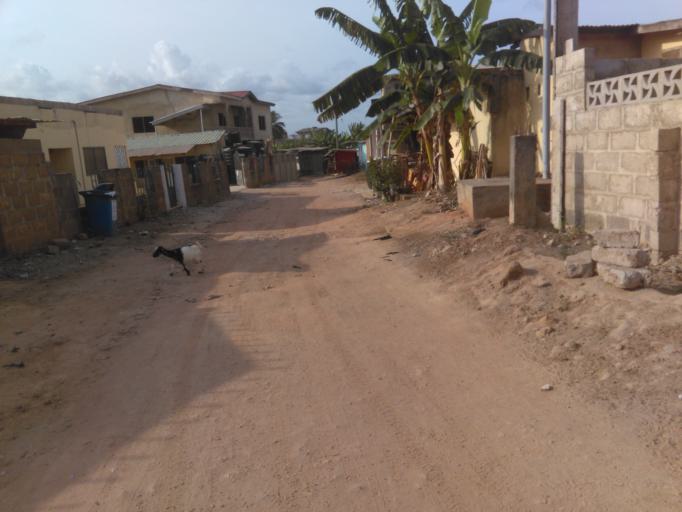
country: GH
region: Central
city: Cape Coast
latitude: 5.1107
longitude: -1.2966
